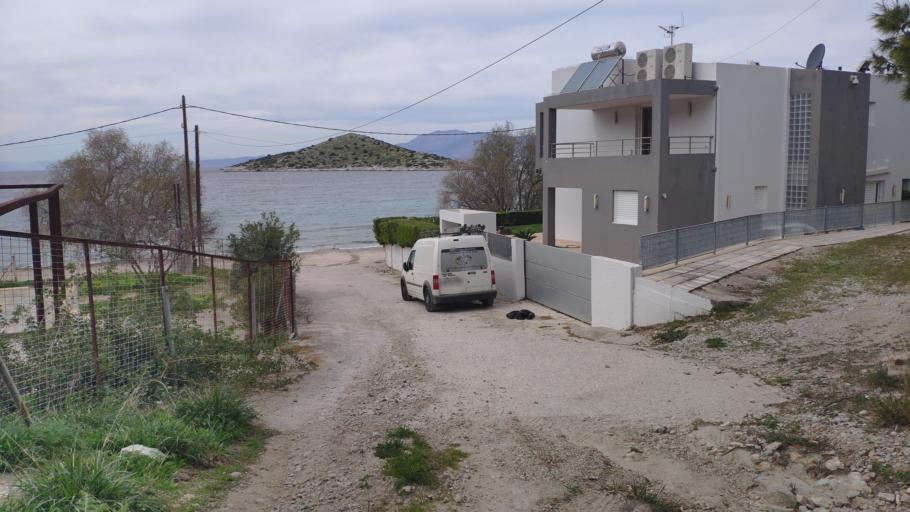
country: GR
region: Attica
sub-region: Nomos Piraios
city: Aianteio
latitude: 37.9004
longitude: 23.4093
